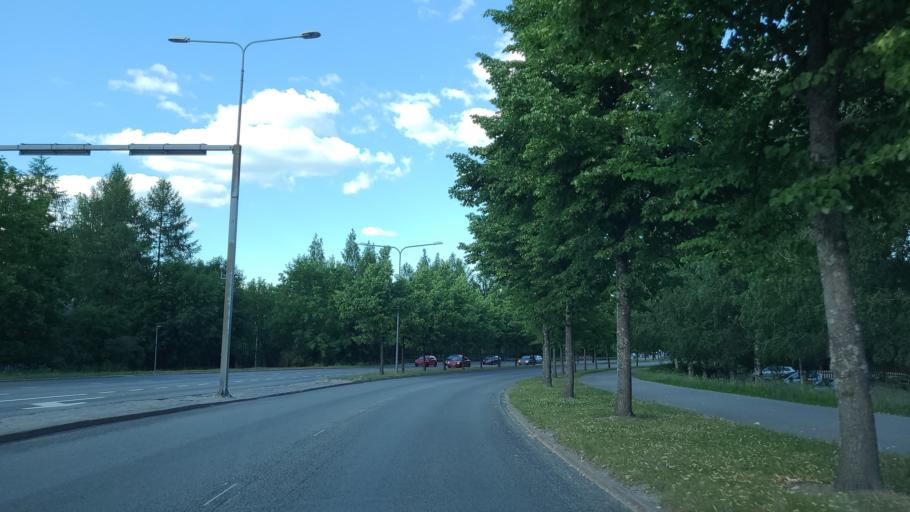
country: FI
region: Central Finland
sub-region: Jyvaeskylae
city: Jyvaeskylae
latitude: 62.2549
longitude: 25.7510
